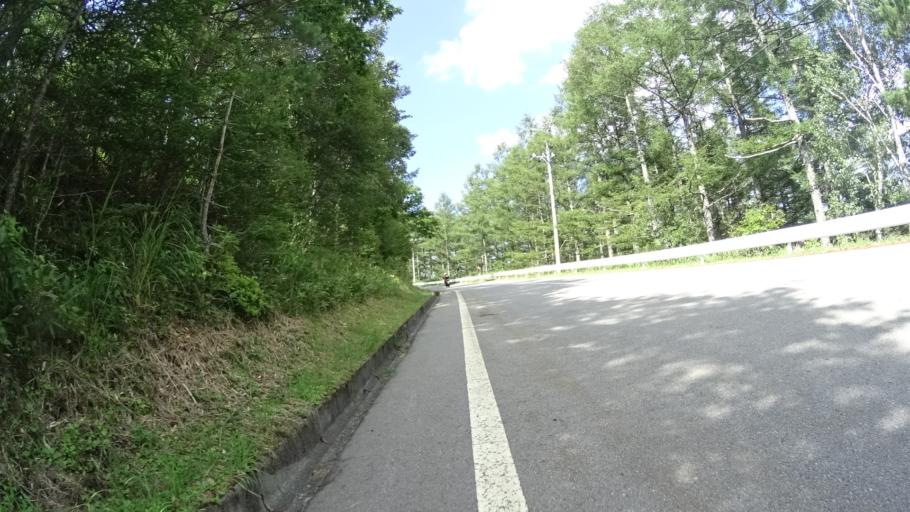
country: JP
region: Nagano
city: Saku
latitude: 36.0625
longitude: 138.3954
